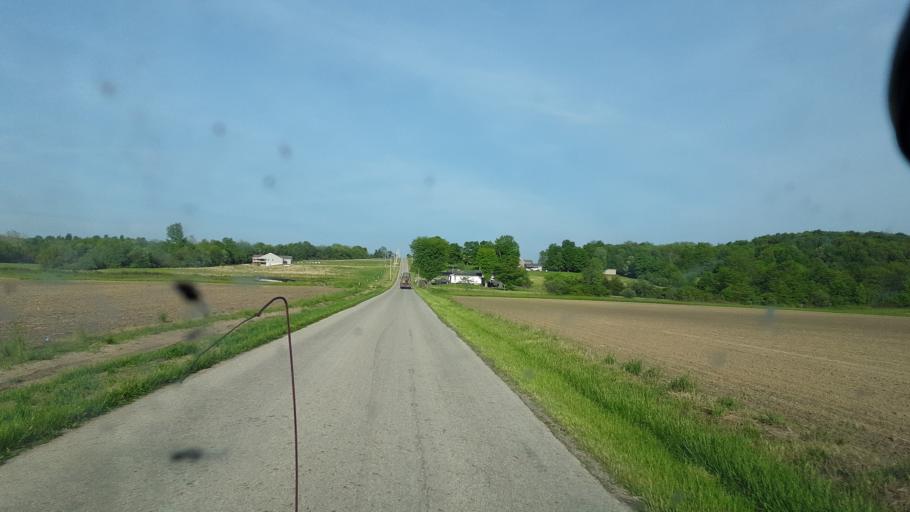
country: US
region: Ohio
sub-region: Ross County
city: Kingston
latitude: 39.5127
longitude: -82.7654
